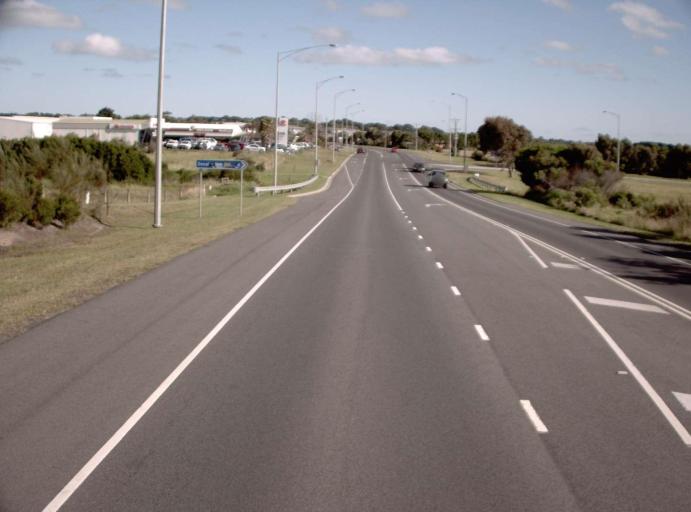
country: AU
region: Victoria
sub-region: Bass Coast
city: North Wonthaggi
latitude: -38.5826
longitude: 145.5755
